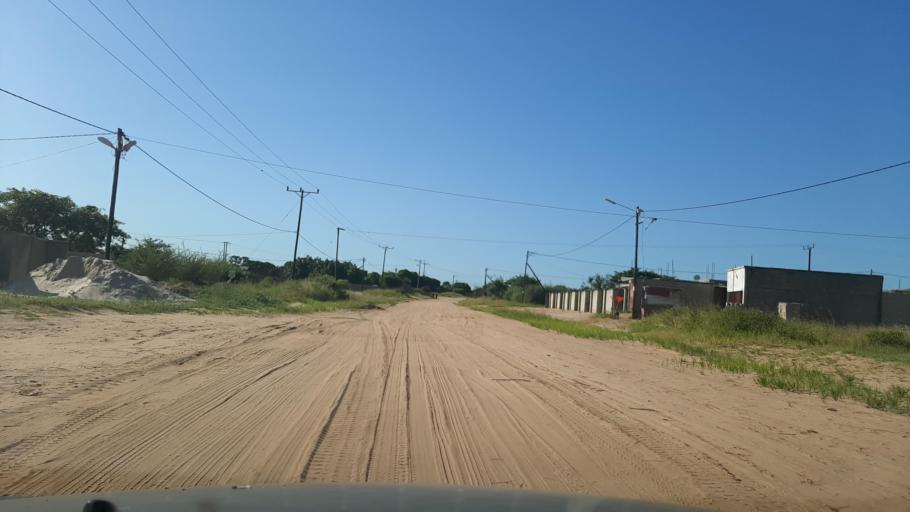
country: MZ
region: Maputo City
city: Maputo
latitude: -25.7664
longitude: 32.5476
